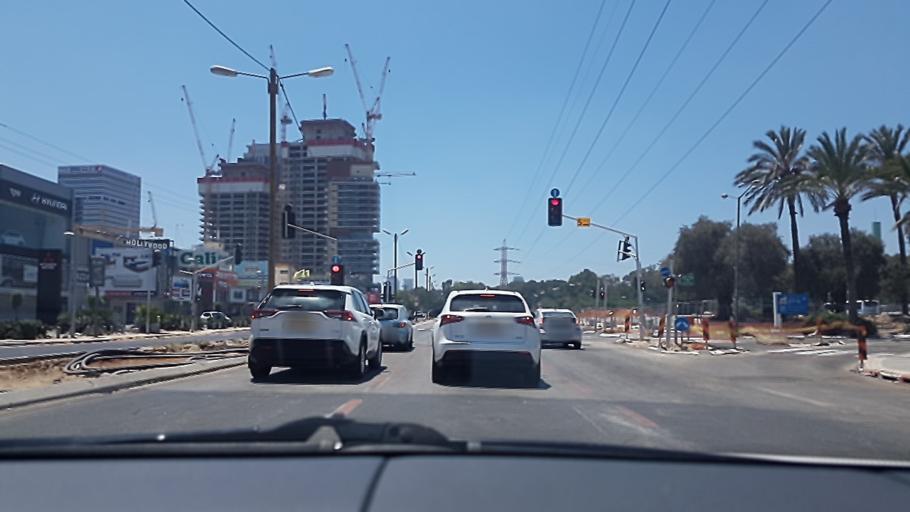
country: IL
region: Tel Aviv
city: Bene Beraq
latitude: 32.0984
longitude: 34.8268
